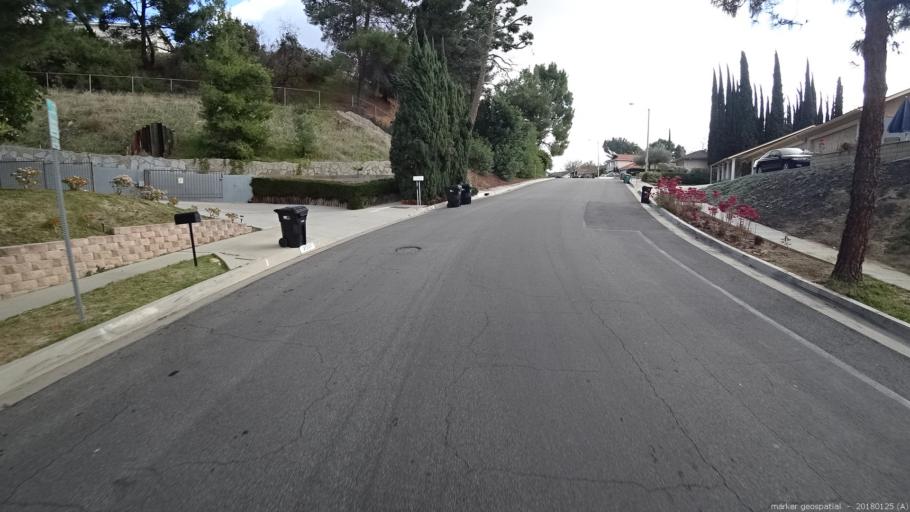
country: US
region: California
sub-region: Los Angeles County
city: Walnut
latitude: 33.9853
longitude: -117.8396
